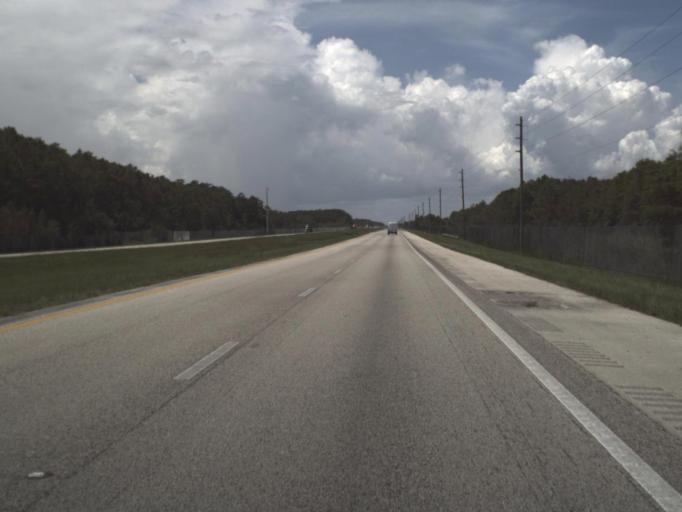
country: US
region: Florida
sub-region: Collier County
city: Immokalee
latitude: 26.1682
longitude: -81.1149
